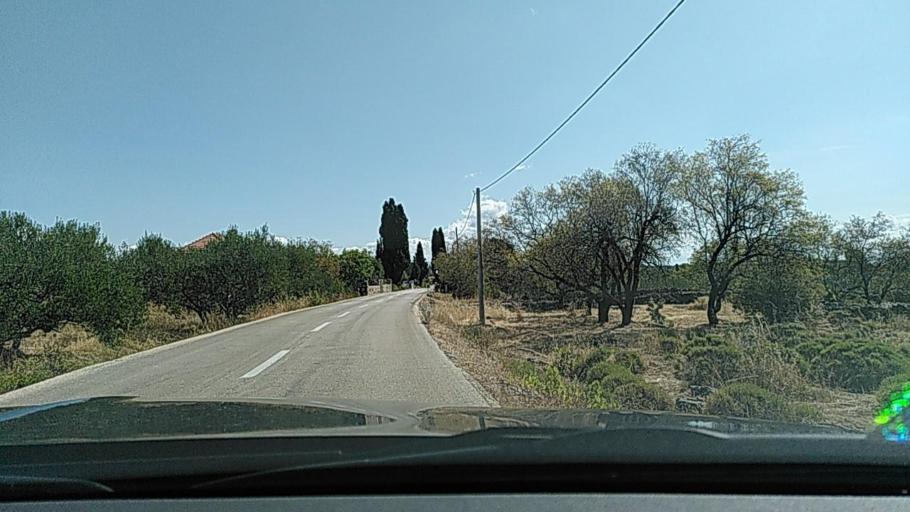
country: HR
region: Splitsko-Dalmatinska
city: Tucepi
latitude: 43.1306
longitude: 16.9852
